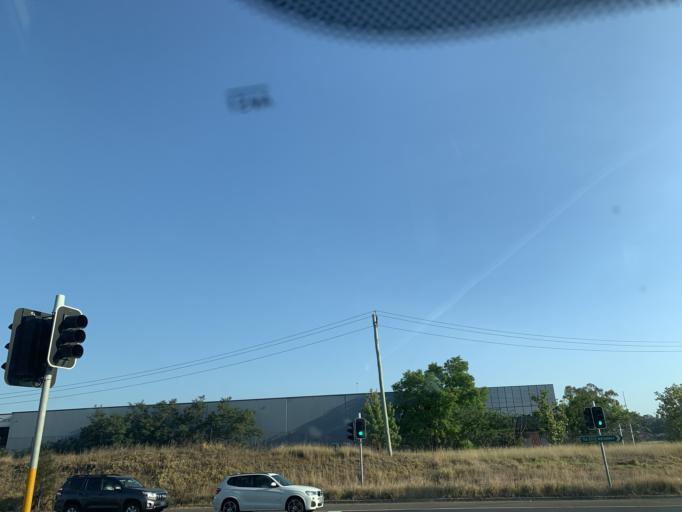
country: AU
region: New South Wales
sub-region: Blacktown
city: Doonside
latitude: -33.7956
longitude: 150.8886
